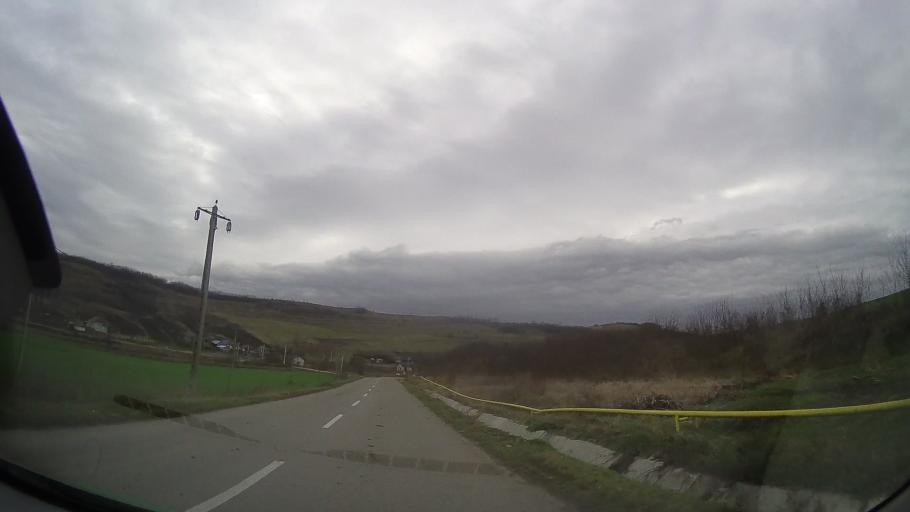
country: RO
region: Bistrita-Nasaud
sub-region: Comuna Milas
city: Milas
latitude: 46.8157
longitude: 24.4389
